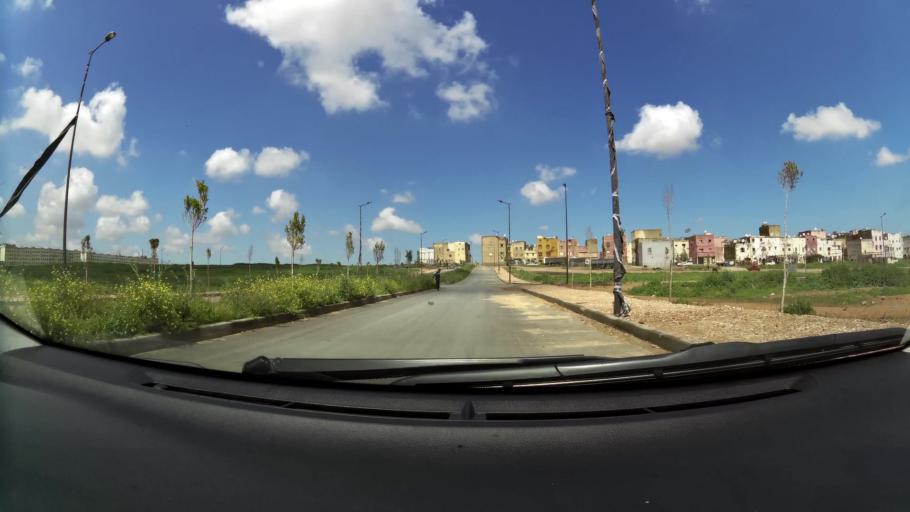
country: MA
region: Grand Casablanca
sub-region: Mediouna
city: Tit Mellil
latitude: 33.5413
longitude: -7.5462
